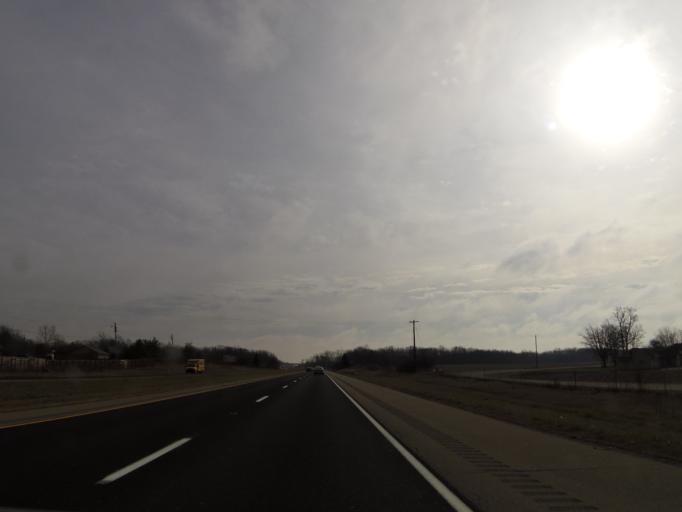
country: US
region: Indiana
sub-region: Hancock County
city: New Palestine
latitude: 39.6519
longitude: -85.9248
